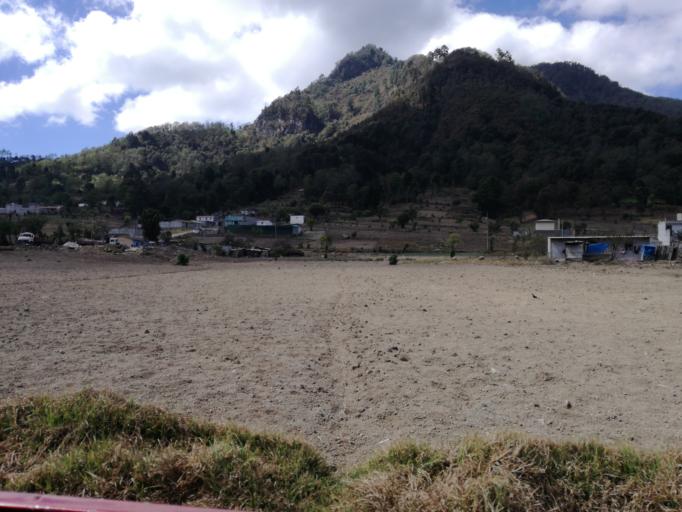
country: GT
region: Quetzaltenango
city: Almolonga
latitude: 14.7844
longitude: -91.5376
